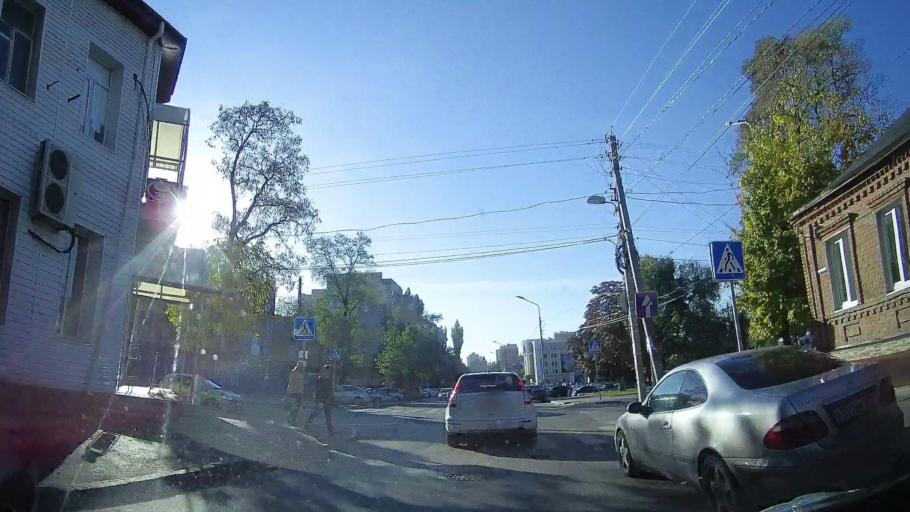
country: RU
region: Rostov
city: Rostov-na-Donu
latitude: 47.2293
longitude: 39.6979
